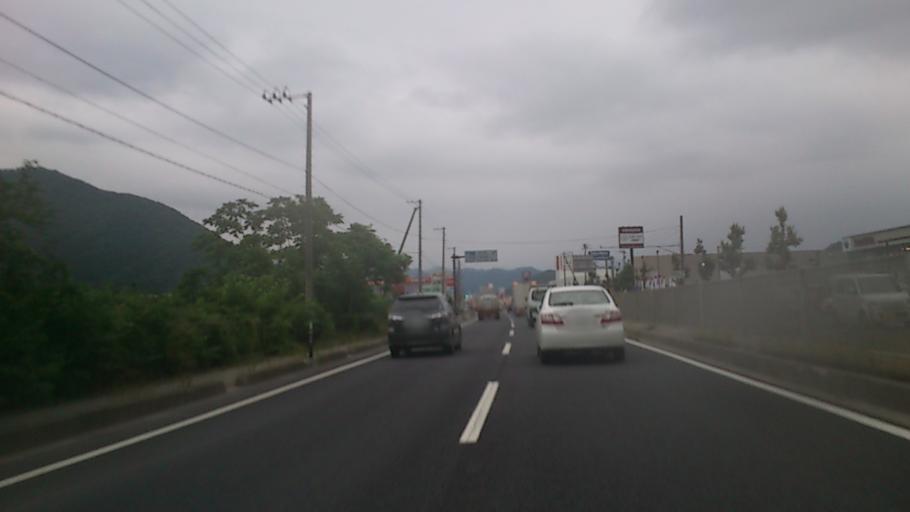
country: JP
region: Yamagata
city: Tendo
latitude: 38.3719
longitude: 140.3836
